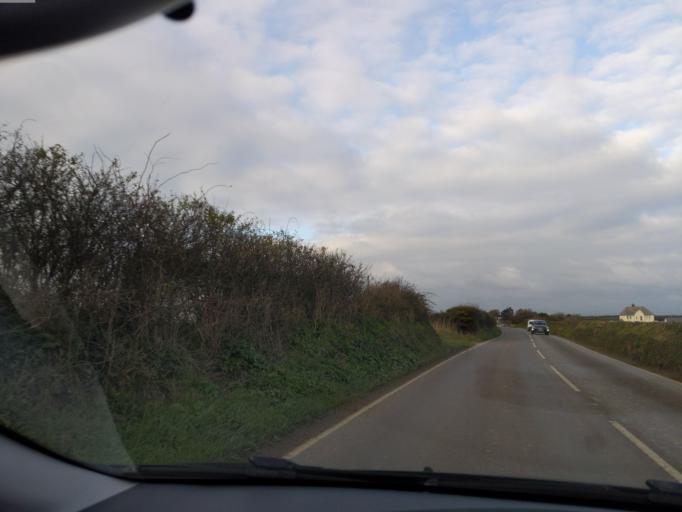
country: GB
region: England
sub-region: Cornwall
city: Padstow
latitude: 50.5197
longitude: -4.9513
